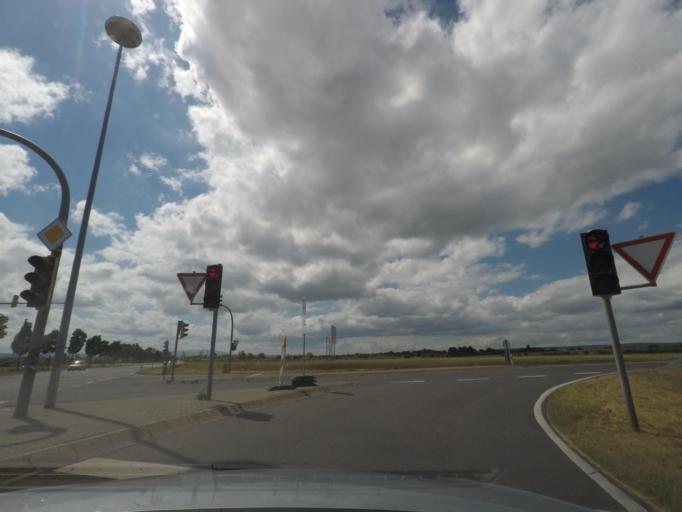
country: DE
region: Saxony-Anhalt
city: Gross Quenstedt
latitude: 51.9073
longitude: 11.0969
